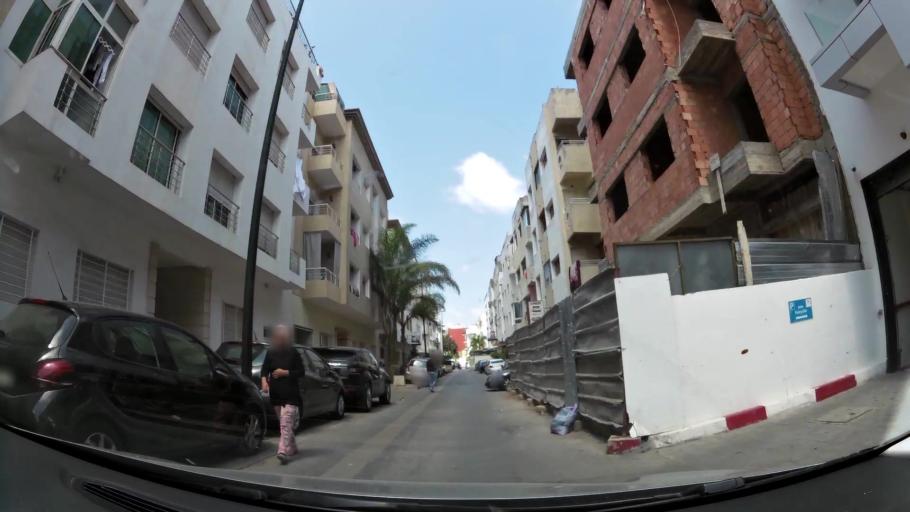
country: MA
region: Rabat-Sale-Zemmour-Zaer
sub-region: Rabat
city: Rabat
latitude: 34.0031
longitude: -6.8506
